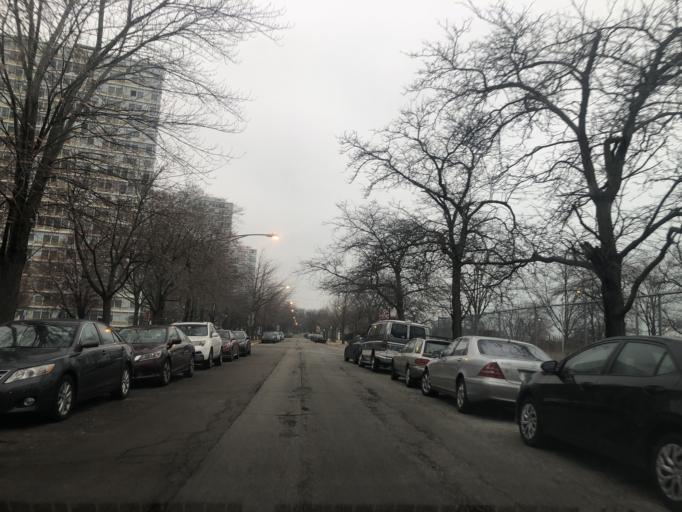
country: US
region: Illinois
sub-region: Cook County
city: Chicago
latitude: 41.8405
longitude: -87.6157
